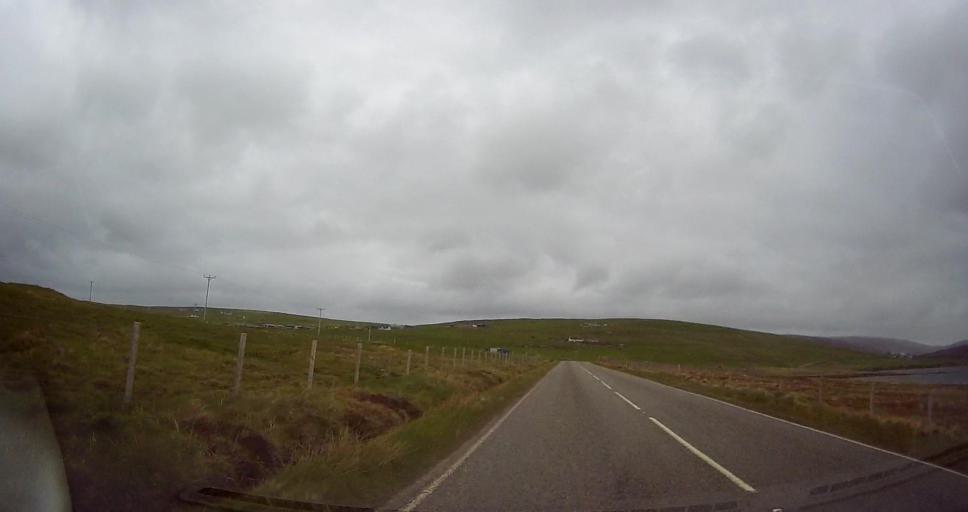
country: GB
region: Scotland
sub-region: Shetland Islands
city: Lerwick
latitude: 60.2569
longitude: -1.4257
